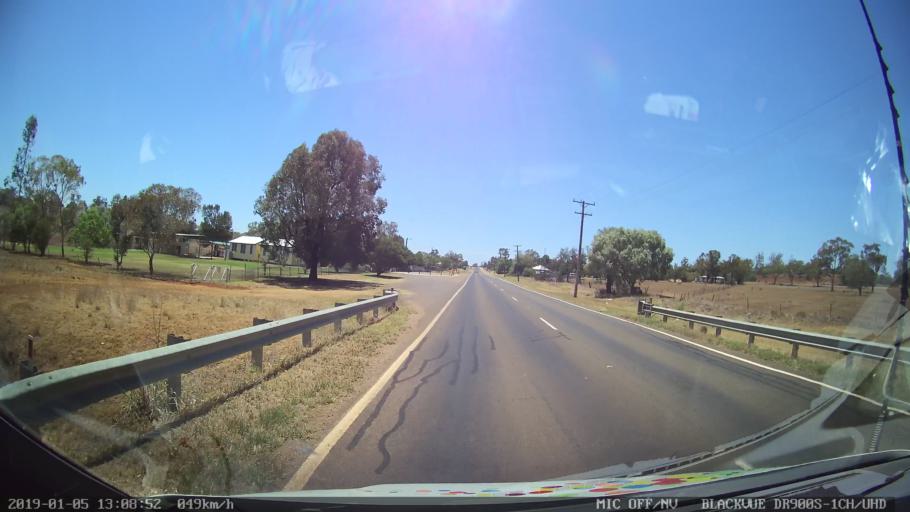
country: AU
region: New South Wales
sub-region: Gunnedah
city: Gunnedah
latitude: -31.0997
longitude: 149.9059
